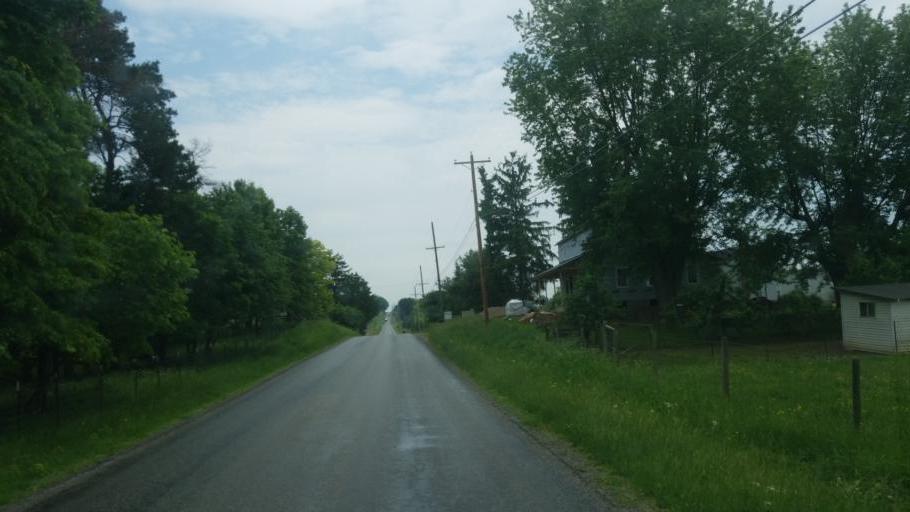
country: US
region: Ohio
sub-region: Wayne County
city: Orrville
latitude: 40.7869
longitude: -81.7552
